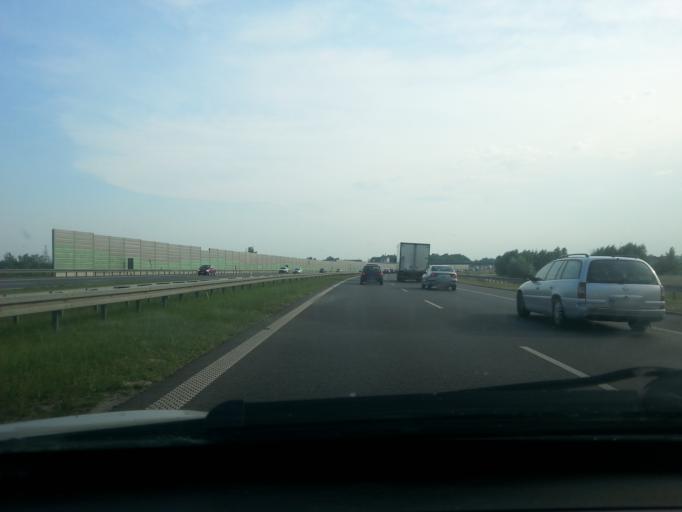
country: PL
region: Masovian Voivodeship
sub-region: Powiat warszawski zachodni
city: Ozarow Mazowiecki
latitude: 52.1800
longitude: 20.7709
